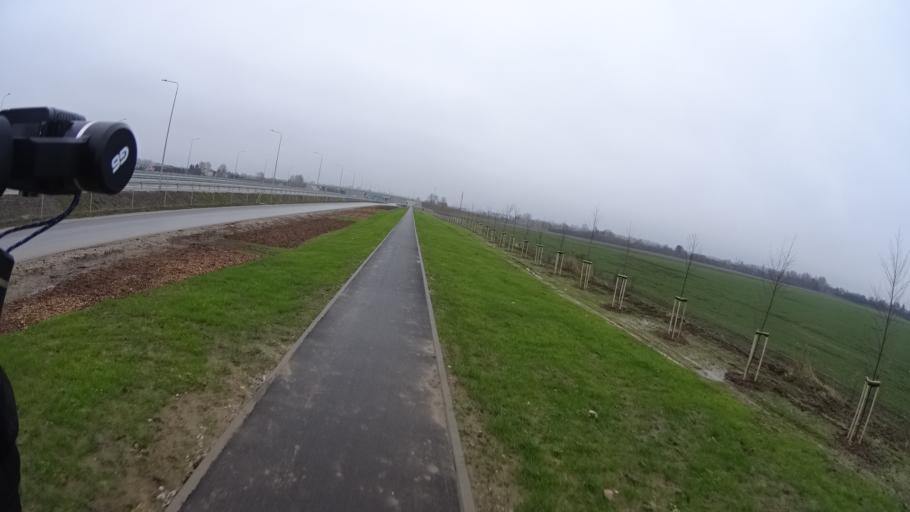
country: PL
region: Masovian Voivodeship
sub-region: Warszawa
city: Wilanow
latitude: 52.1540
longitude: 21.1171
